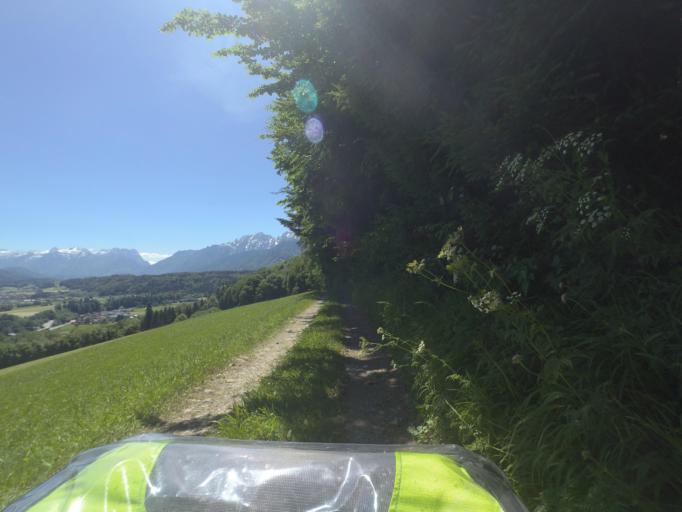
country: AT
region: Salzburg
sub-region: Politischer Bezirk Hallein
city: Oberalm
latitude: 47.7113
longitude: 13.1174
